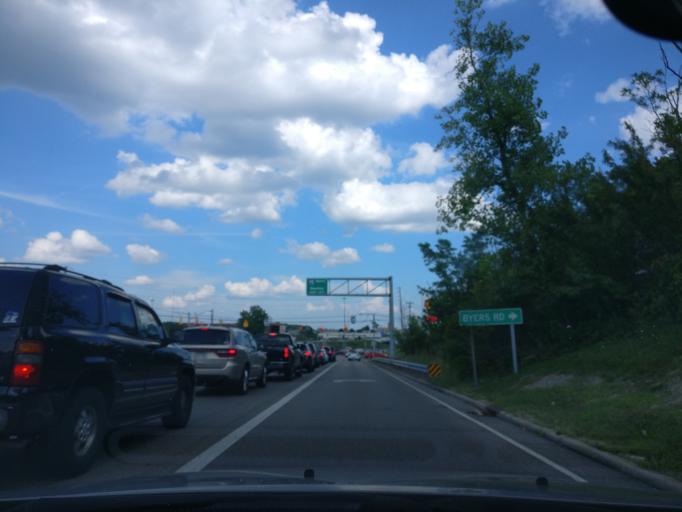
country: US
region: Ohio
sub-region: Montgomery County
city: West Carrollton City
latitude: 39.6401
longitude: -84.2365
